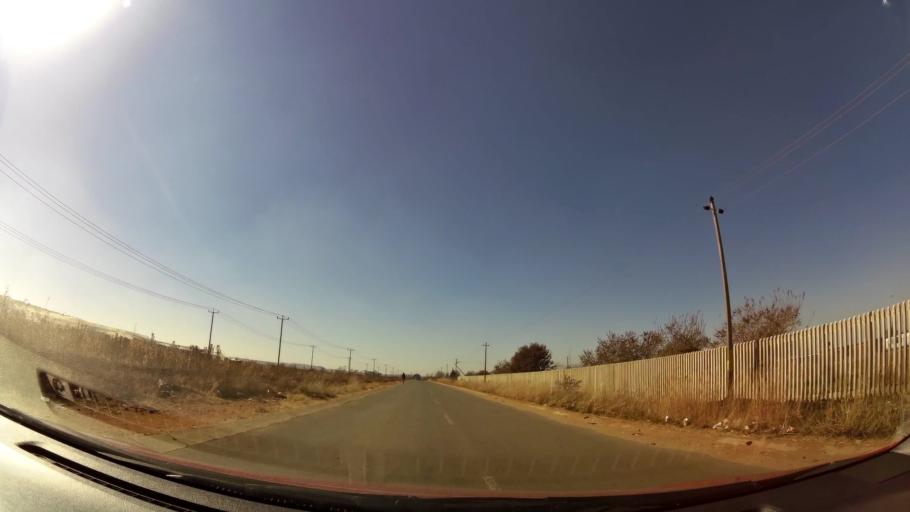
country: ZA
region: Gauteng
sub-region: City of Johannesburg Metropolitan Municipality
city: Soweto
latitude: -26.2154
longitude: 27.8272
